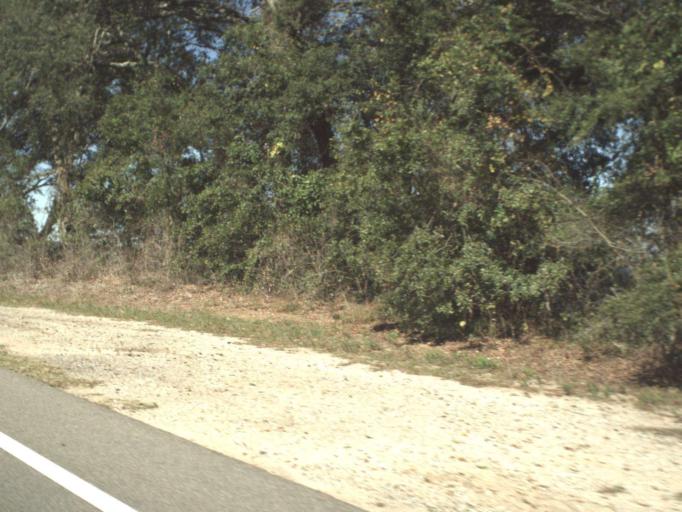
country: US
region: Florida
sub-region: Escambia County
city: Ferry Pass
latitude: 30.5181
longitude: -87.1686
